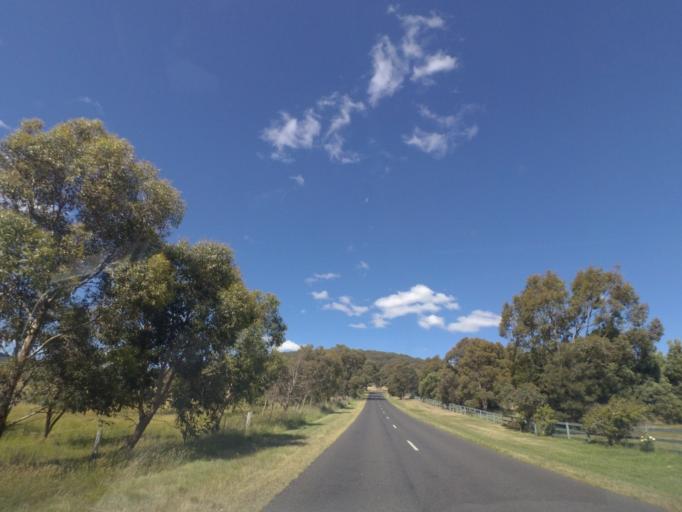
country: AU
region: Victoria
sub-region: Hume
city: Sunbury
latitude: -37.4291
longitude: 144.6137
